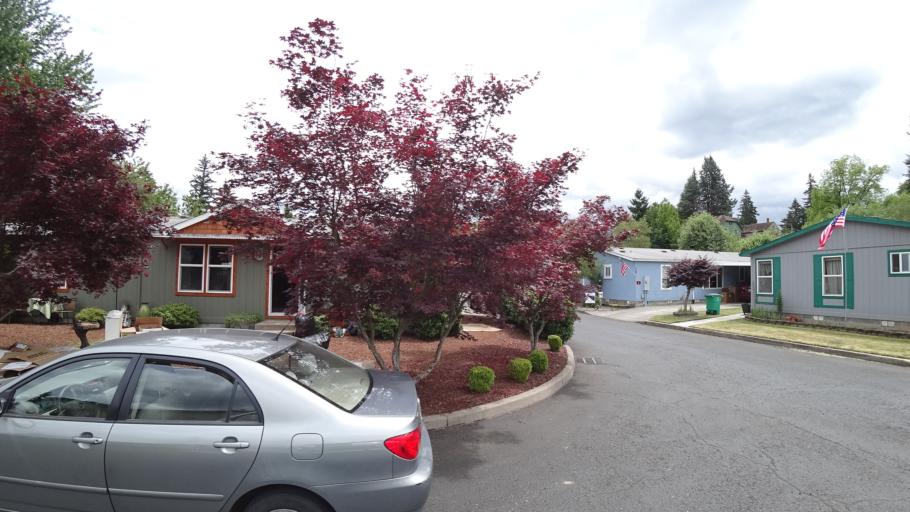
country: US
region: Oregon
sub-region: Clackamas County
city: Happy Valley
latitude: 45.4851
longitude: -122.5272
